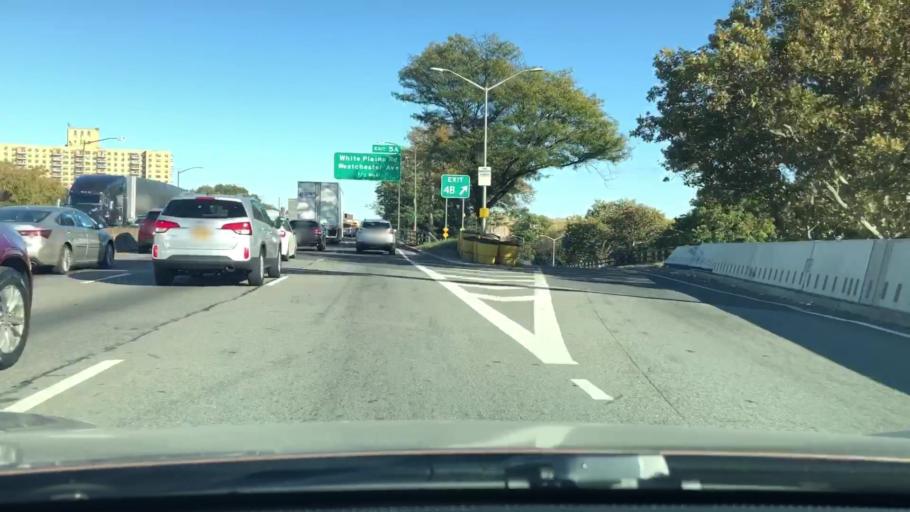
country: US
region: New York
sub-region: Bronx
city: The Bronx
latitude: 40.8364
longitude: -73.8765
